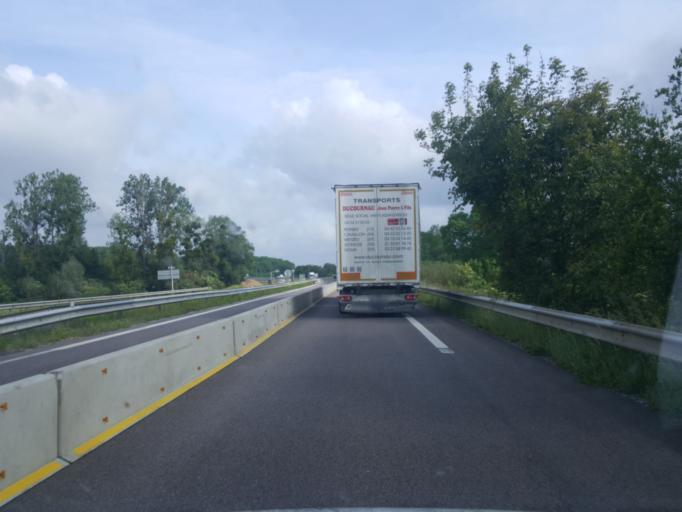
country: FR
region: Haute-Normandie
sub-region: Departement de l'Eure
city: Heudreville-sur-Eure
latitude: 49.1553
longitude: 1.1824
